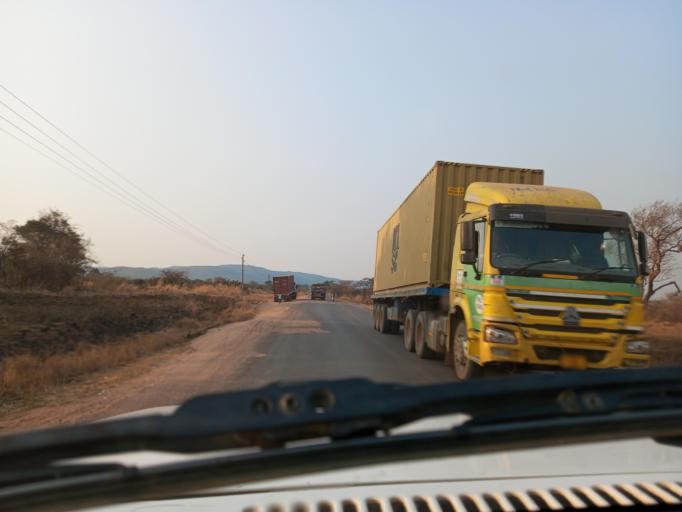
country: ZM
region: Northern
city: Mpika
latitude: -11.9262
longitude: 31.4177
